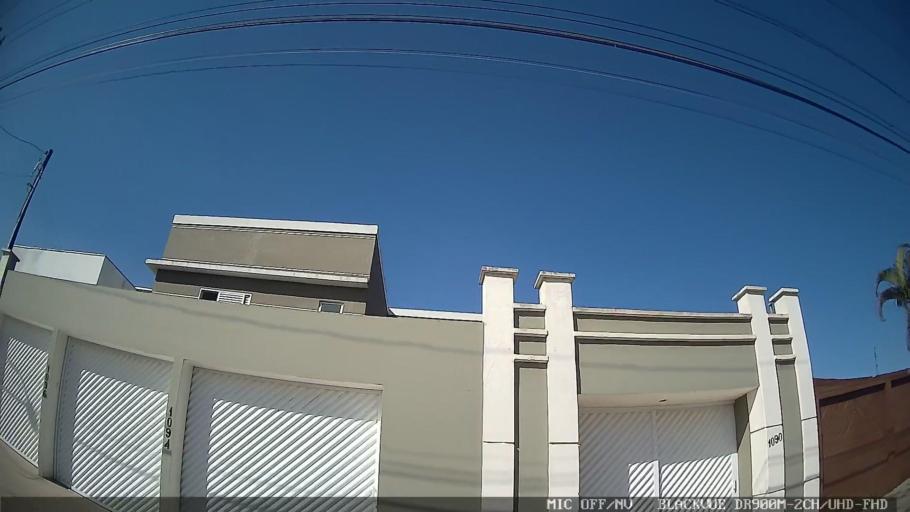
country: BR
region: Sao Paulo
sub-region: Guaruja
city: Guaruja
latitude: -23.9756
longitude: -46.2126
